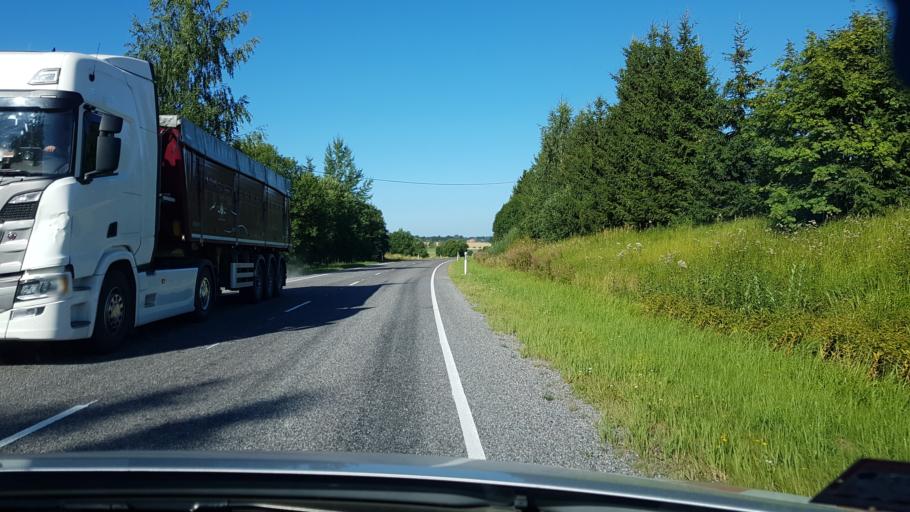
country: EE
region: Tartu
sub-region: Tartu linn
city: Tartu
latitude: 58.4649
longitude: 26.7513
